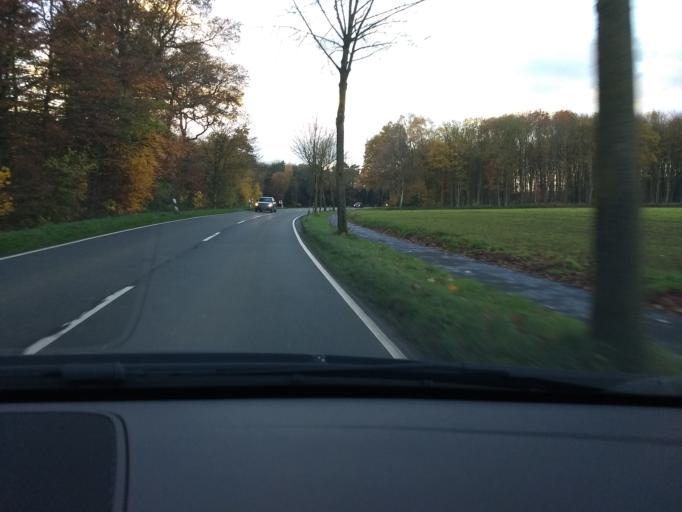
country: DE
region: North Rhine-Westphalia
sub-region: Regierungsbezirk Munster
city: Klein Reken
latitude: 51.7510
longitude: 7.0214
